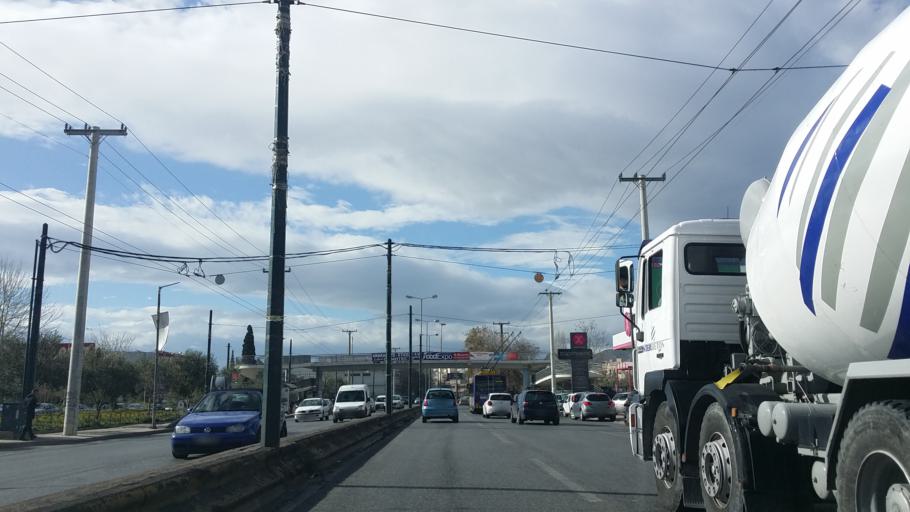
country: GR
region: Attica
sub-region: Nomarchia Athinas
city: Aigaleo
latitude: 37.9763
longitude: 23.6737
